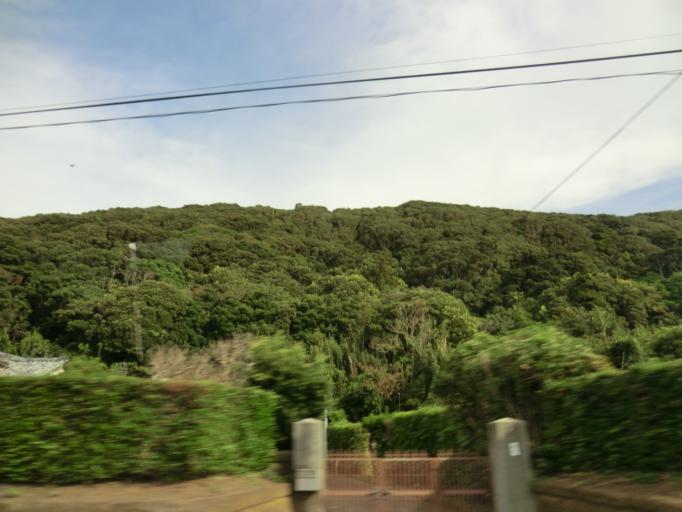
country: JP
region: Chiba
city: Tateyama
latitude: 35.0315
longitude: 139.8362
